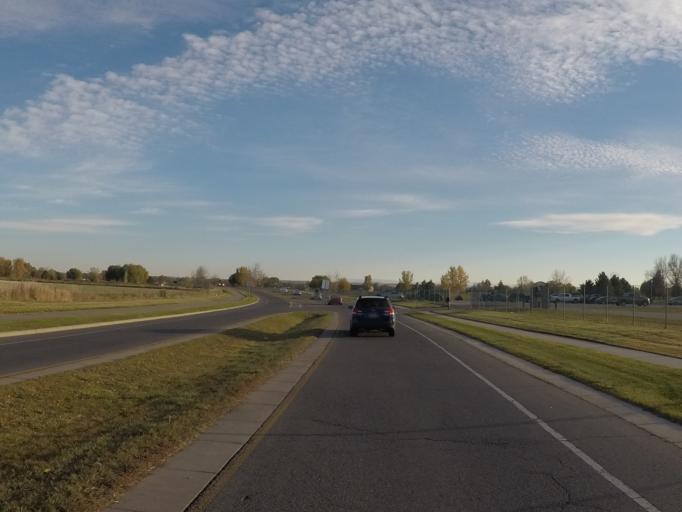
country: US
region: Montana
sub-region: Yellowstone County
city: Billings
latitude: 45.7821
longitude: -108.6005
